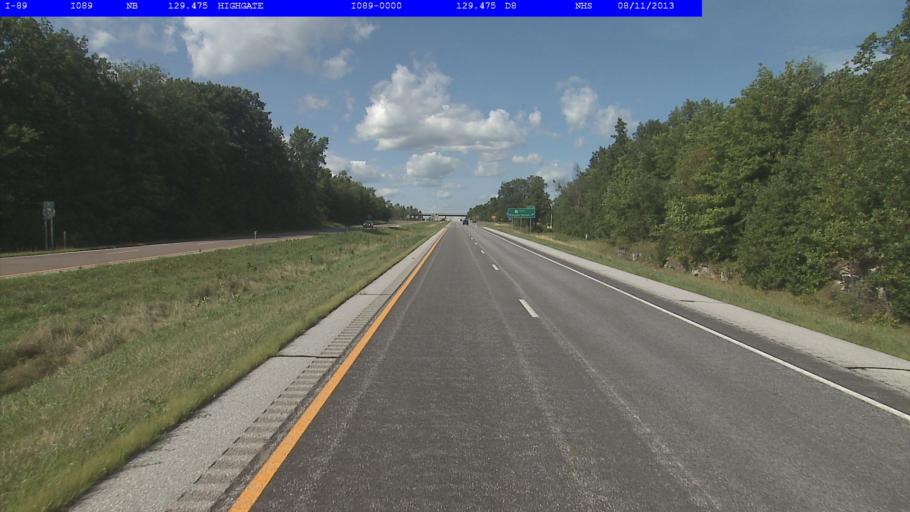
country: US
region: Vermont
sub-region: Franklin County
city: Swanton
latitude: 45.0043
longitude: -73.0866
